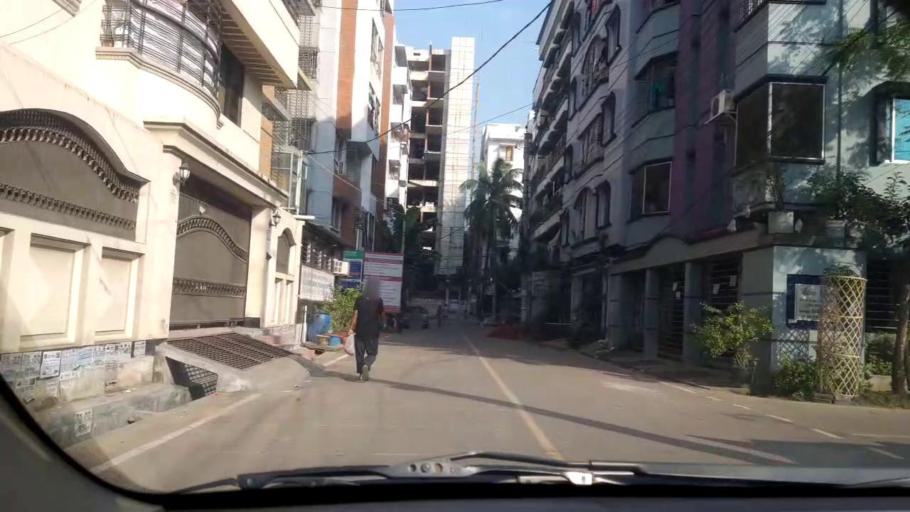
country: BD
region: Dhaka
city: Tungi
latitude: 23.8659
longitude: 90.3891
